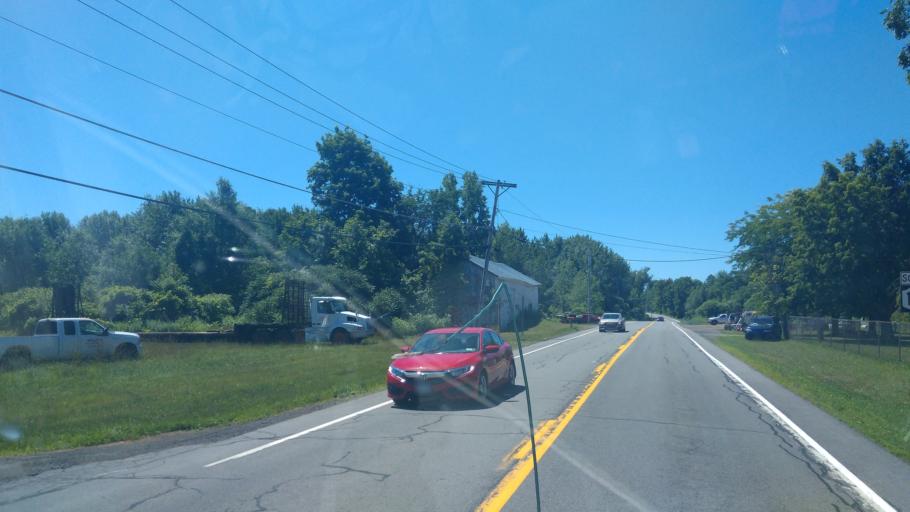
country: US
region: New York
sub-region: Wayne County
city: Sodus
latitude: 43.1760
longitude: -76.9875
